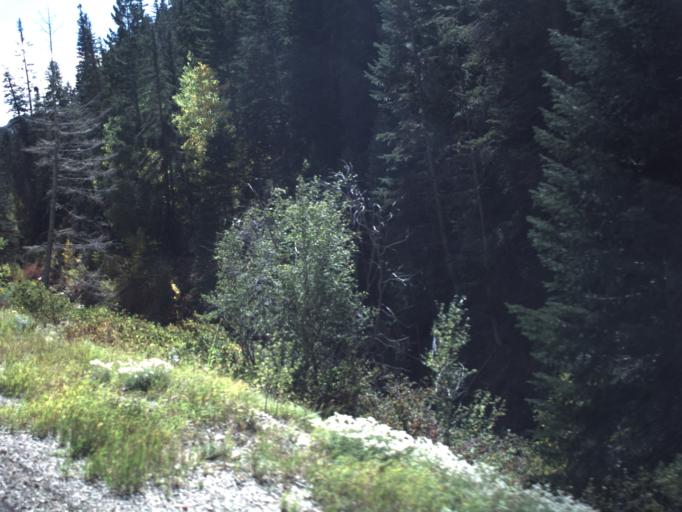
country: US
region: Utah
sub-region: Iron County
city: Cedar City
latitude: 37.6199
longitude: -112.9317
